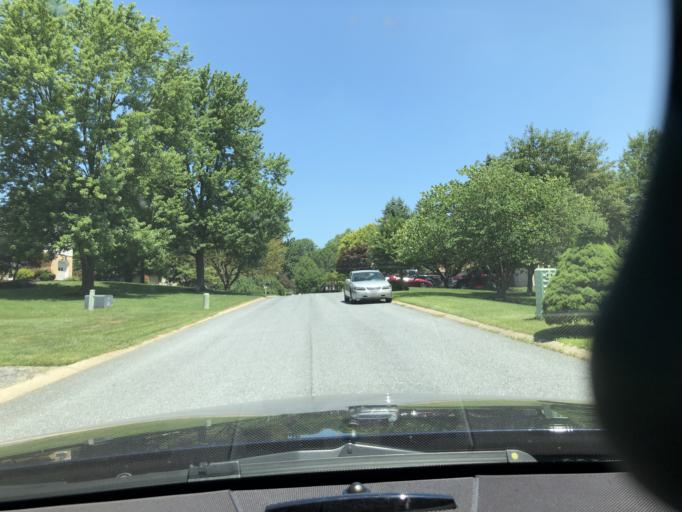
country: US
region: Maryland
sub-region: Carroll County
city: Westminster
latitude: 39.5512
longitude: -76.9698
